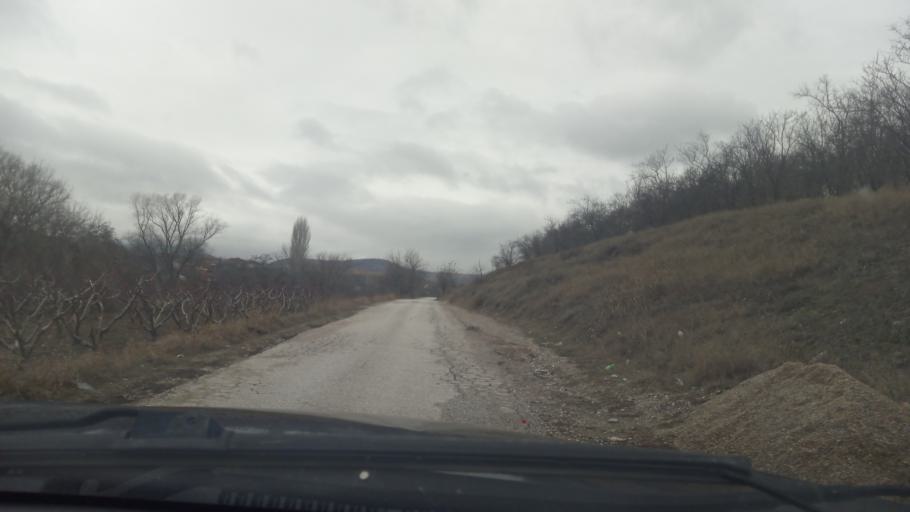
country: MK
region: Gradsko
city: Gradsko
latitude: 41.6001
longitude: 21.9039
